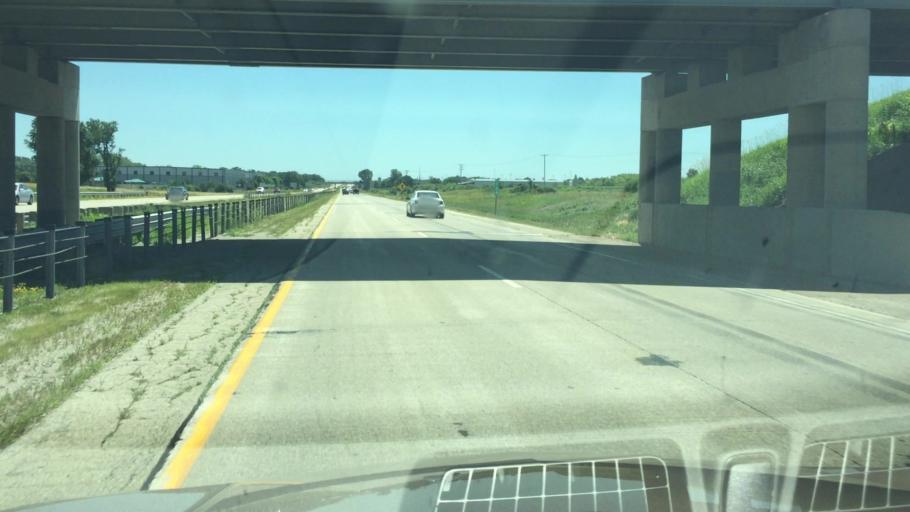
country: US
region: Wisconsin
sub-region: Dodge County
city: Beaver Dam
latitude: 43.4772
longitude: -88.8155
